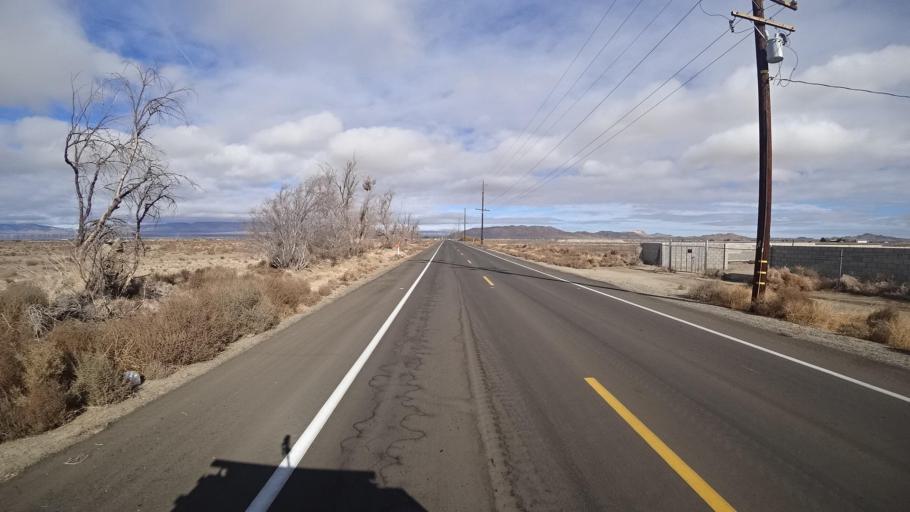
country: US
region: California
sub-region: Kern County
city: Rosamond
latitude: 34.8253
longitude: -118.2906
